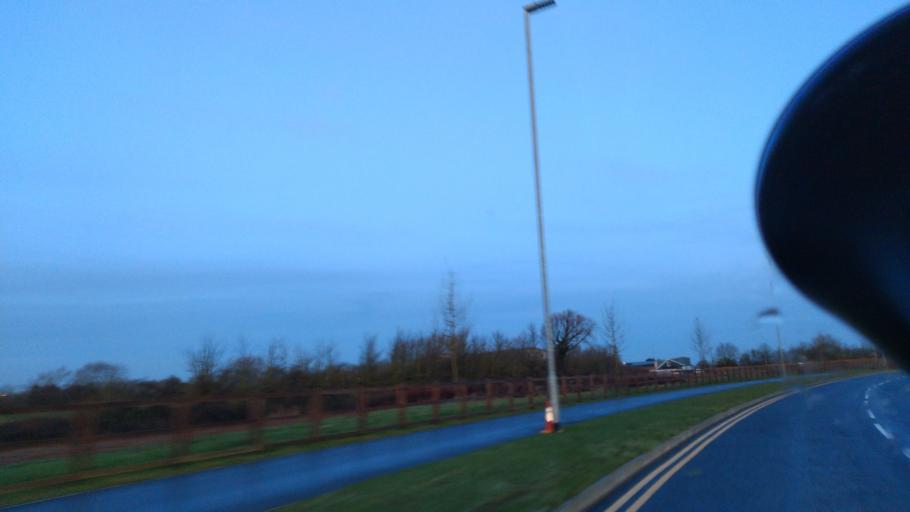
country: GB
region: England
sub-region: Borough of Swindon
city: Wanborough
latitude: 51.5772
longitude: -1.7216
